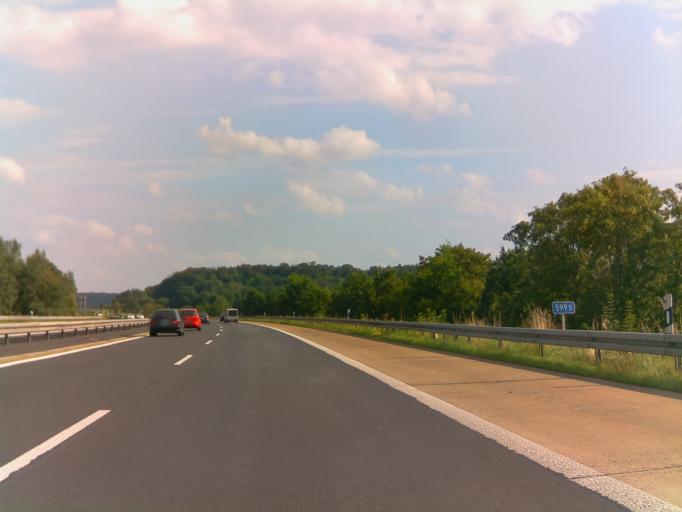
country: DE
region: Bavaria
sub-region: Regierungsbezirk Unterfranken
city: Schondra
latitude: 50.2870
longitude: 9.8548
